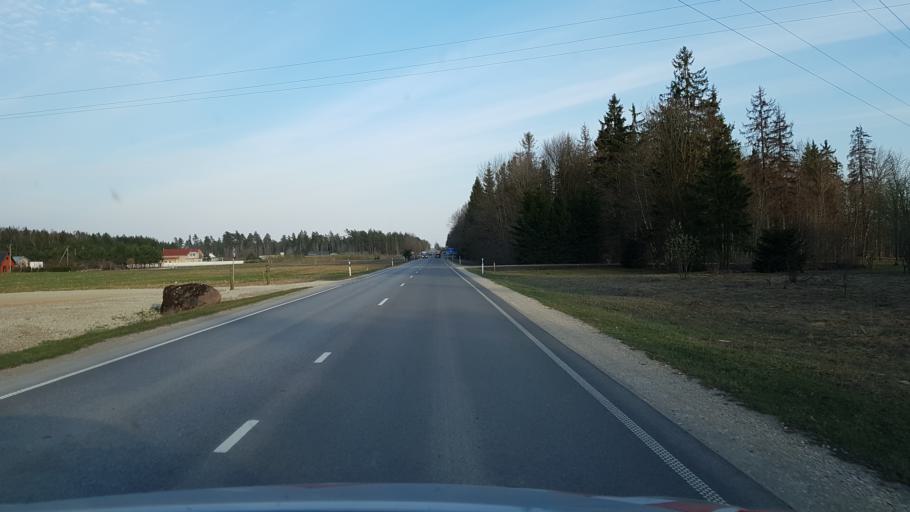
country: EE
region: Laeaene-Virumaa
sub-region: Rakvere linn
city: Rakvere
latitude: 59.3351
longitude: 26.3950
